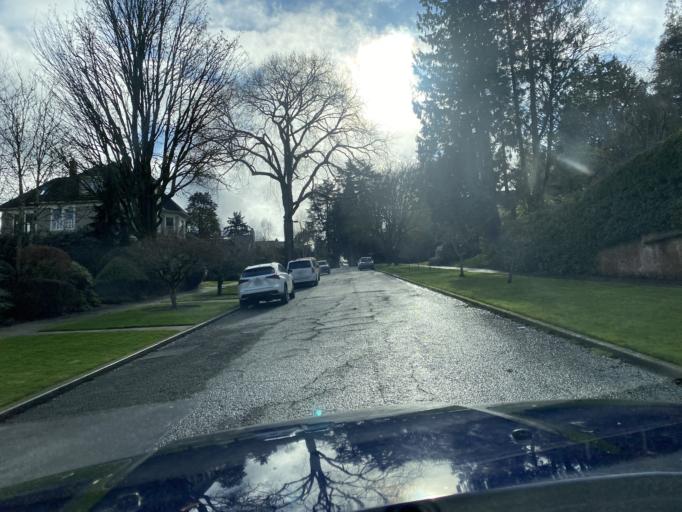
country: US
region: Washington
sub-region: King County
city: Seattle
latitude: 47.6297
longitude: -122.2842
